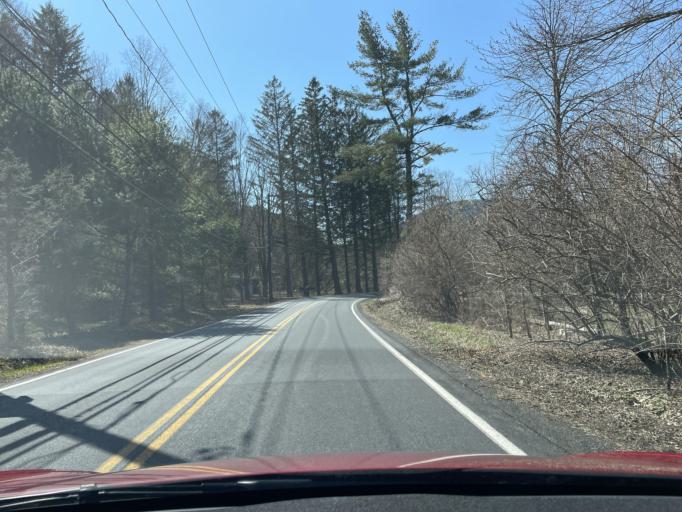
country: US
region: New York
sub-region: Ulster County
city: Shokan
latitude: 42.0288
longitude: -74.1859
